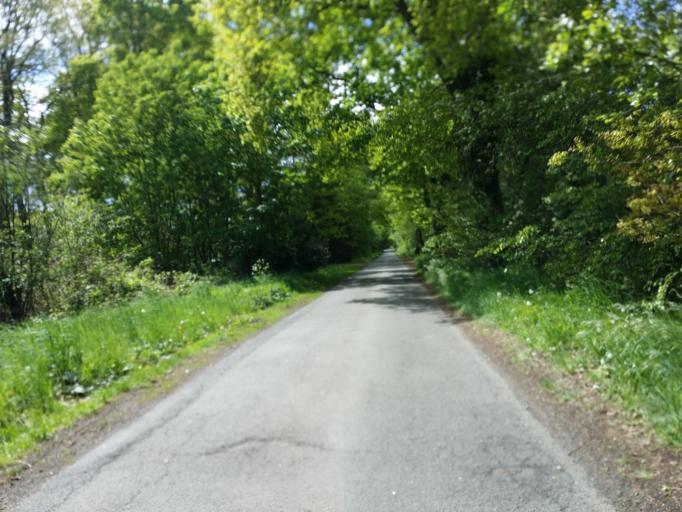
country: DE
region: Lower Saxony
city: Gross Ippener
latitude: 52.9867
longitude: 8.6184
